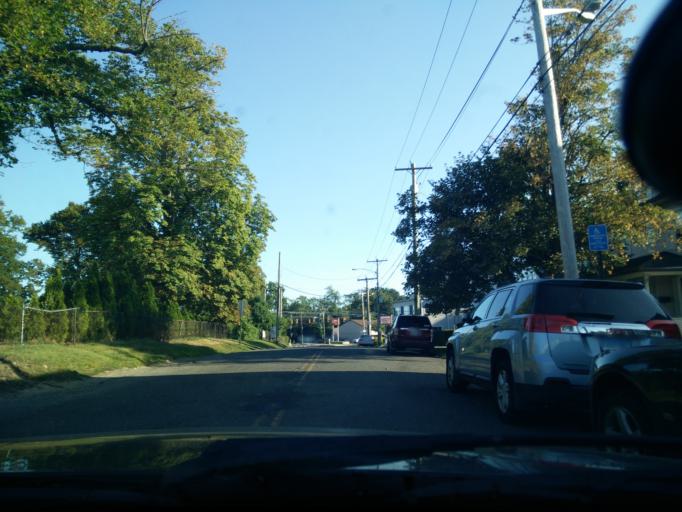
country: US
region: Connecticut
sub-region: Fairfield County
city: Bridgeport
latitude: 41.1618
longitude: -73.2236
